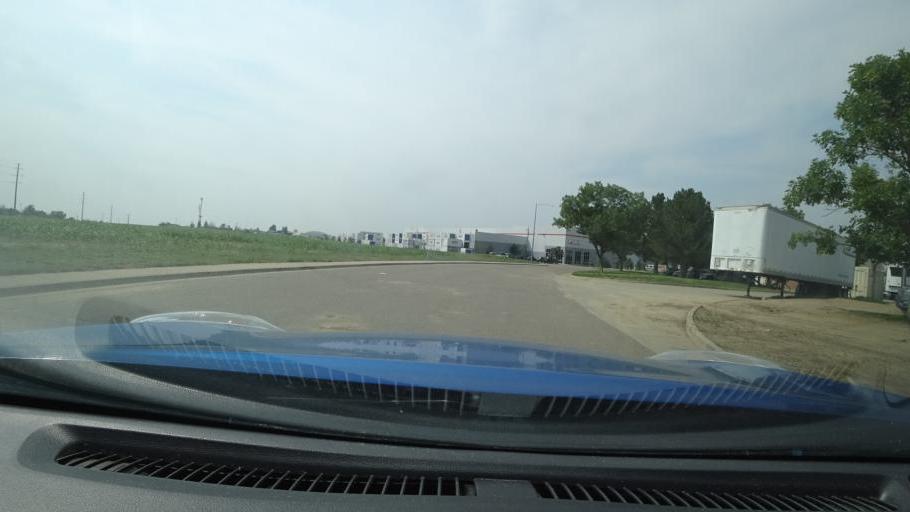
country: US
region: Colorado
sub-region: Adams County
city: Aurora
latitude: 39.7556
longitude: -104.7427
